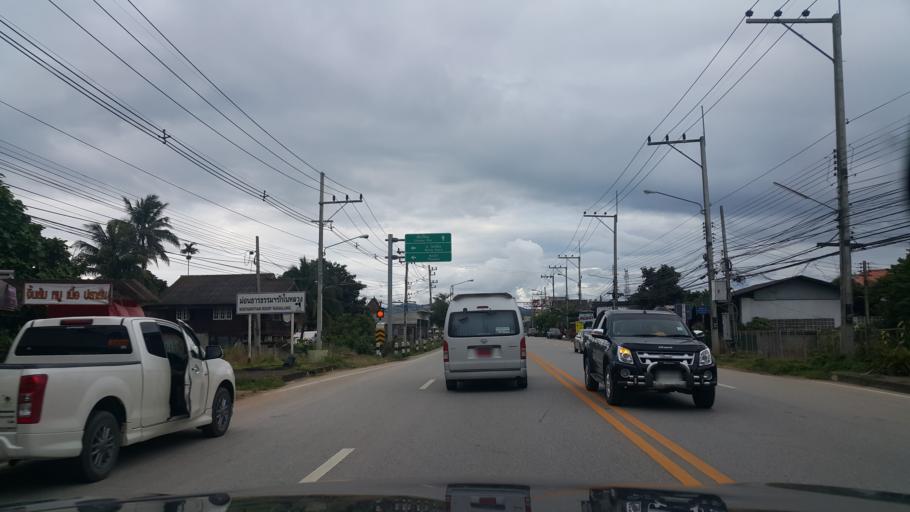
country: TH
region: Lampang
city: Wang Nuea
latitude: 19.2131
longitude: 99.5177
